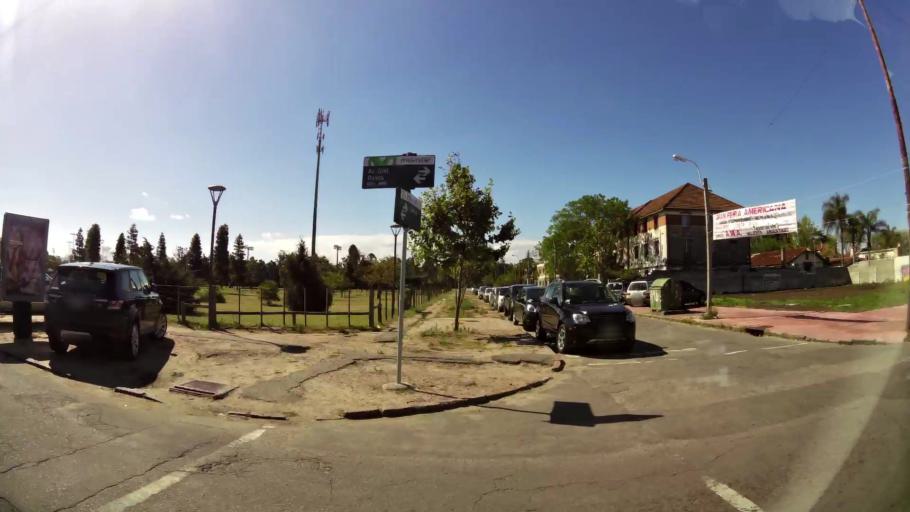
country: UY
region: Canelones
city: Paso de Carrasco
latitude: -34.8858
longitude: -56.0573
